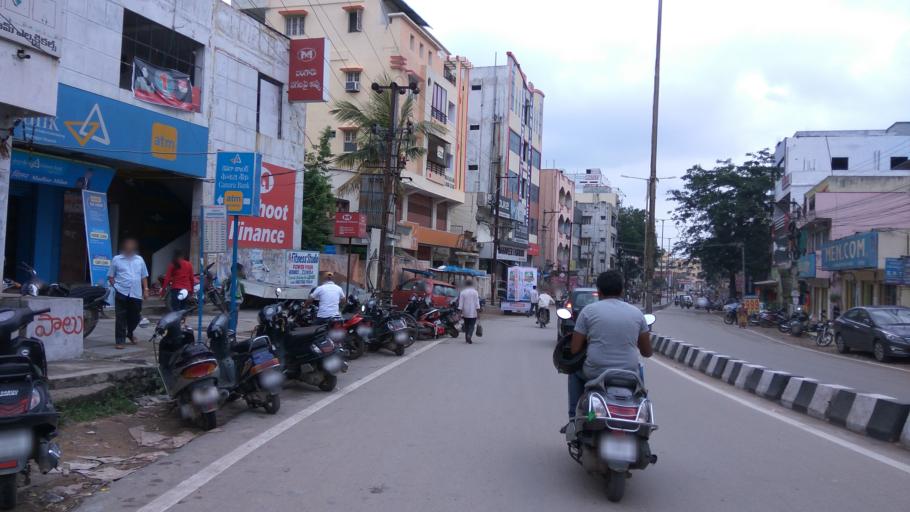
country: IN
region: Telangana
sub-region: Hyderabad
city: Malkajgiri
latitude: 17.4524
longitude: 78.5336
